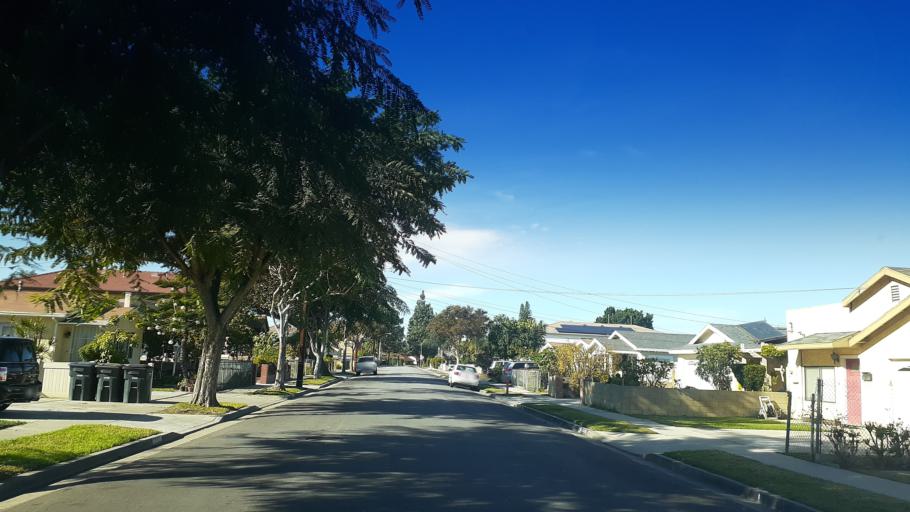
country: US
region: California
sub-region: Los Angeles County
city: Cerritos
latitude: 33.8556
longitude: -118.0700
